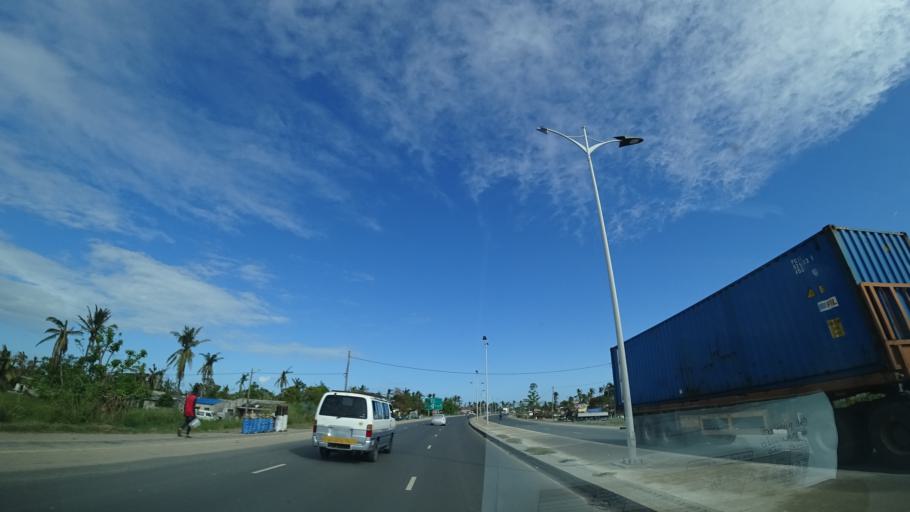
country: MZ
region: Sofala
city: Beira
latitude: -19.7714
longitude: 34.8832
